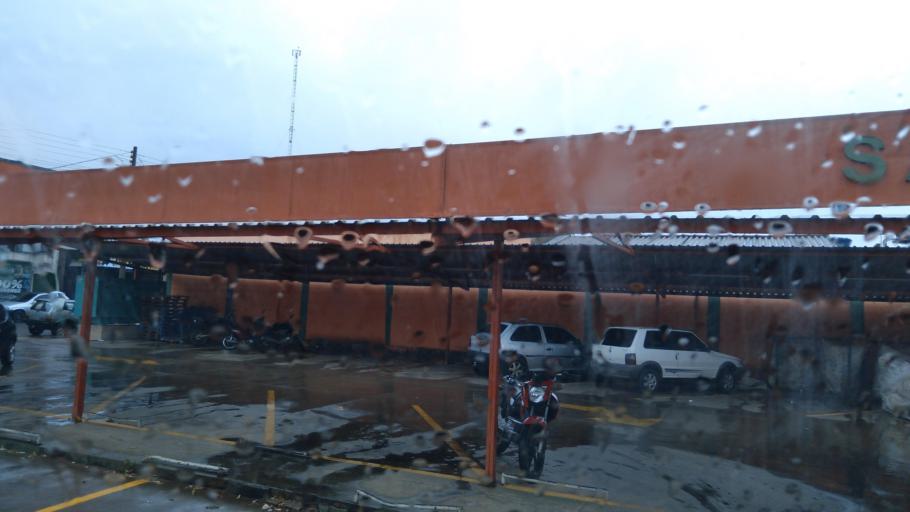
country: BR
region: Goias
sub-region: Mineiros
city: Mineiros
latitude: -17.5391
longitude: -52.5425
